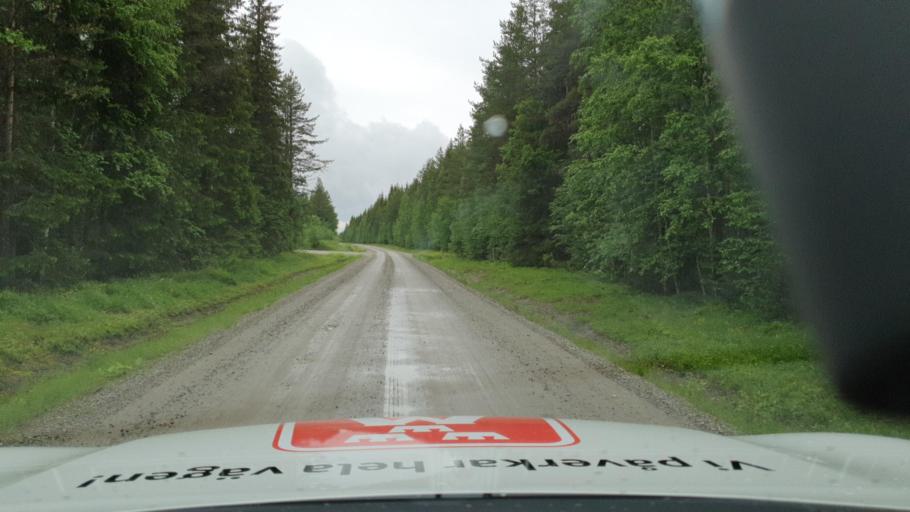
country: SE
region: Vaesterbotten
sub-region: Dorotea Kommun
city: Dorotea
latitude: 64.0781
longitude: 16.6901
